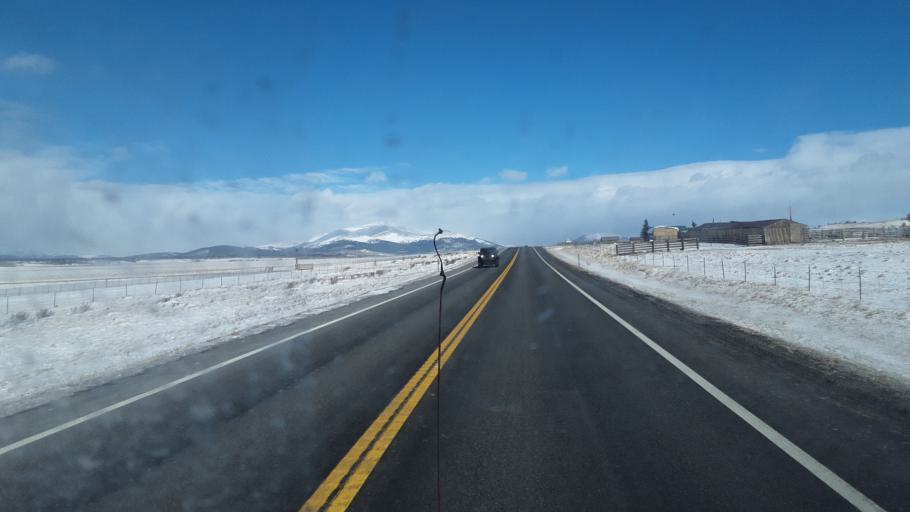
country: US
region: Colorado
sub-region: Park County
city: Fairplay
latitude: 39.1751
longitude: -106.0006
